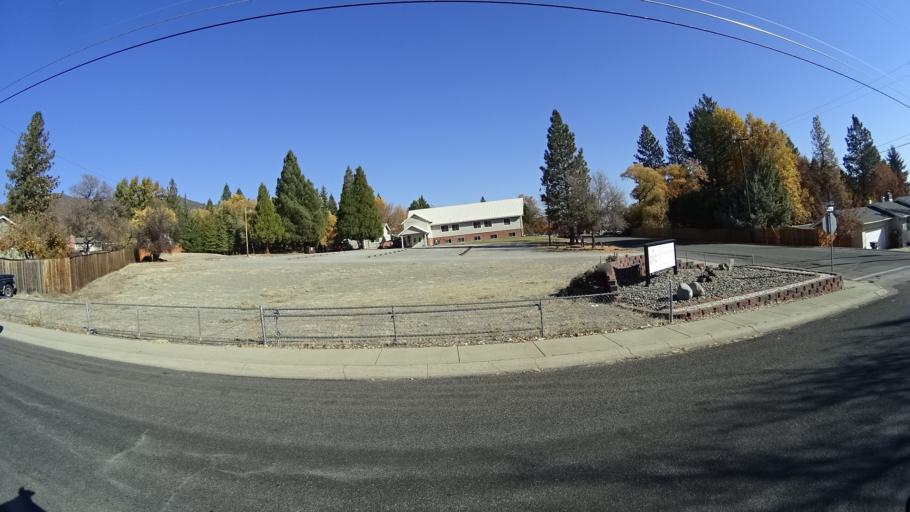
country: US
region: California
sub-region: Siskiyou County
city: Yreka
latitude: 41.7377
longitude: -122.6558
